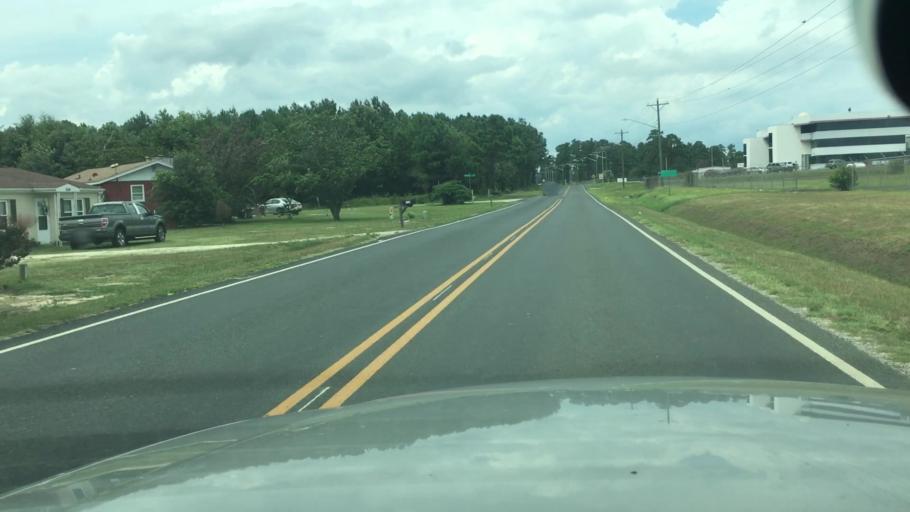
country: US
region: North Carolina
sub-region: Cumberland County
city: Hope Mills
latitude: 34.9878
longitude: -78.8905
